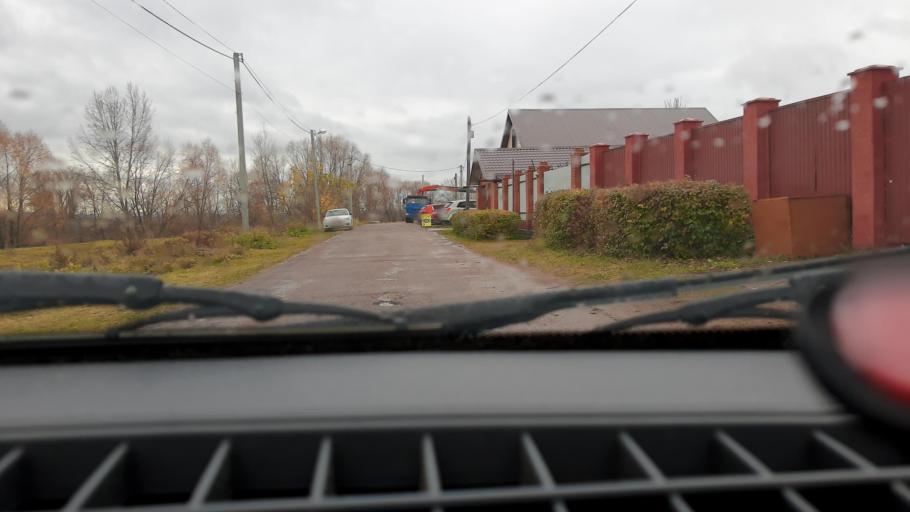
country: RU
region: Bashkortostan
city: Ufa
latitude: 54.8204
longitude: 55.9917
